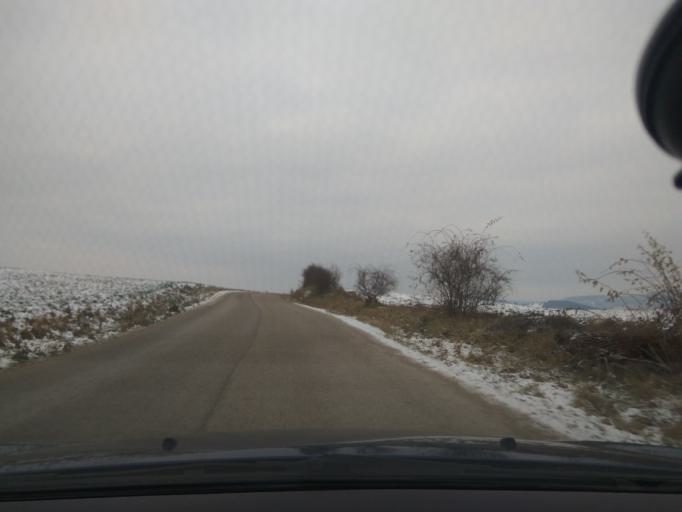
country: SK
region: Nitriansky
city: Stara Tura
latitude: 48.7924
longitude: 17.7290
